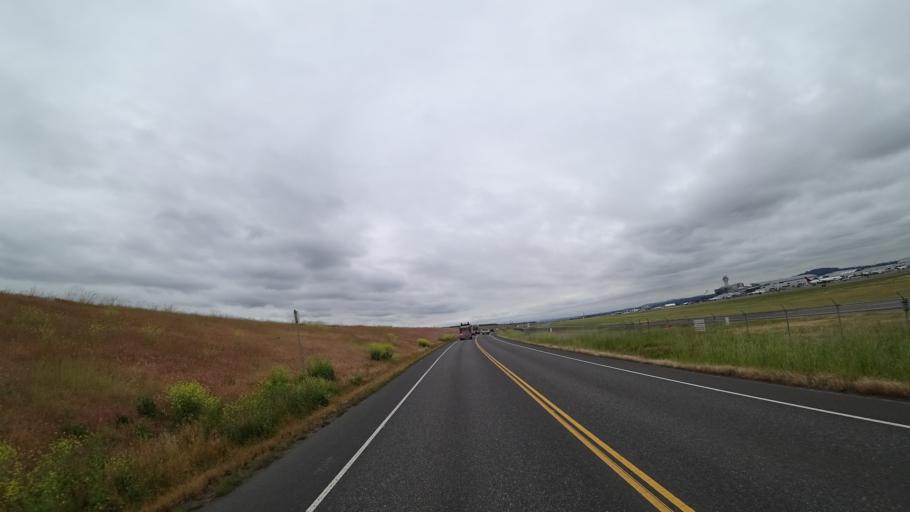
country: US
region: Washington
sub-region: Clark County
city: Walnut Grove
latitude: 45.5982
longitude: -122.5998
